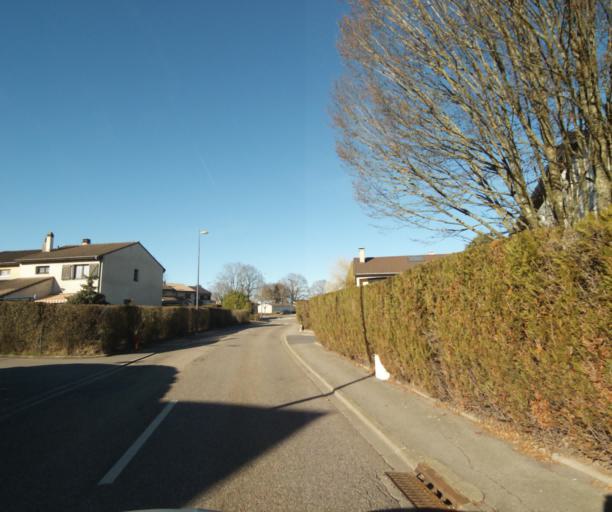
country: FR
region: Lorraine
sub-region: Departement de Meurthe-et-Moselle
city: Heillecourt
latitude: 48.6426
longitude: 6.2003
